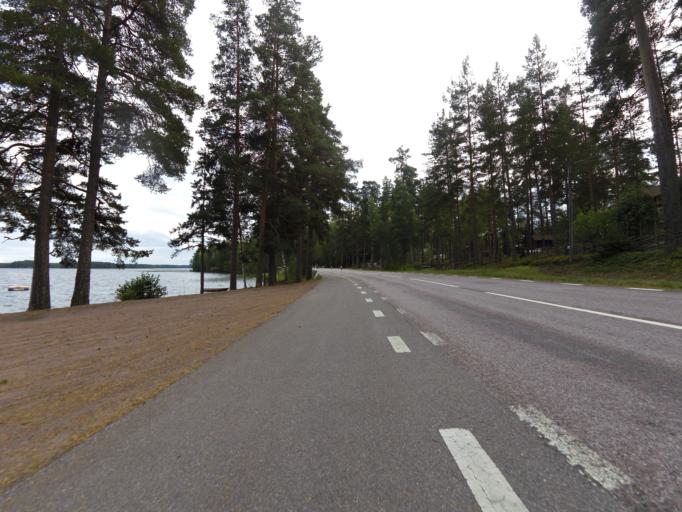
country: SE
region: Gaevleborg
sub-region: Sandvikens Kommun
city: Sandviken
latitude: 60.7038
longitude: 16.8122
